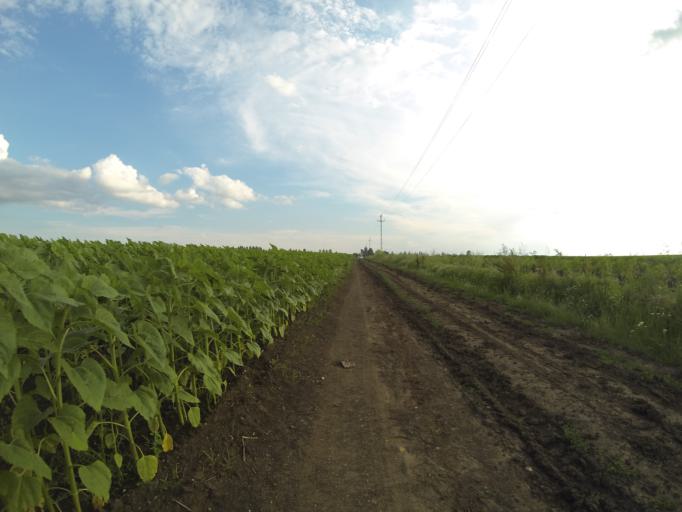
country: RO
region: Dolj
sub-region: Comuna Caloparu
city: Salcuta
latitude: 44.1468
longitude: 23.6981
